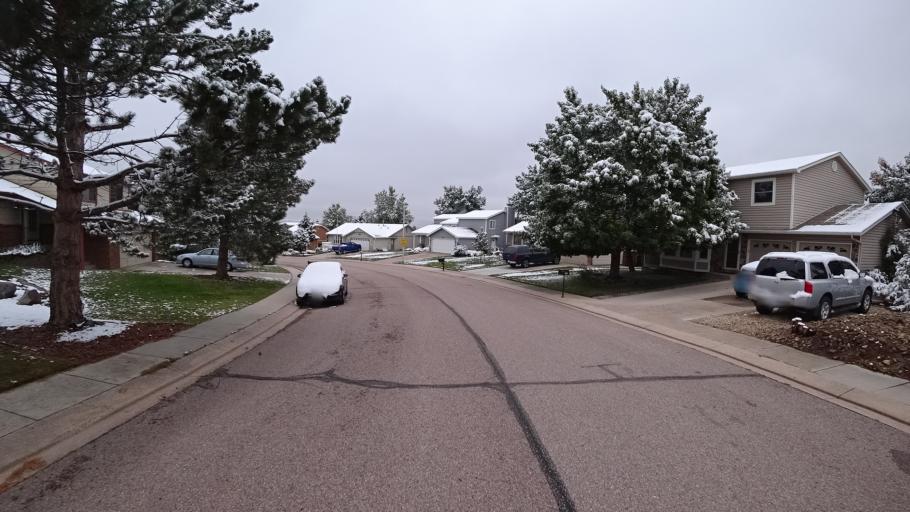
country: US
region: Colorado
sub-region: El Paso County
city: Colorado Springs
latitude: 38.9244
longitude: -104.7778
